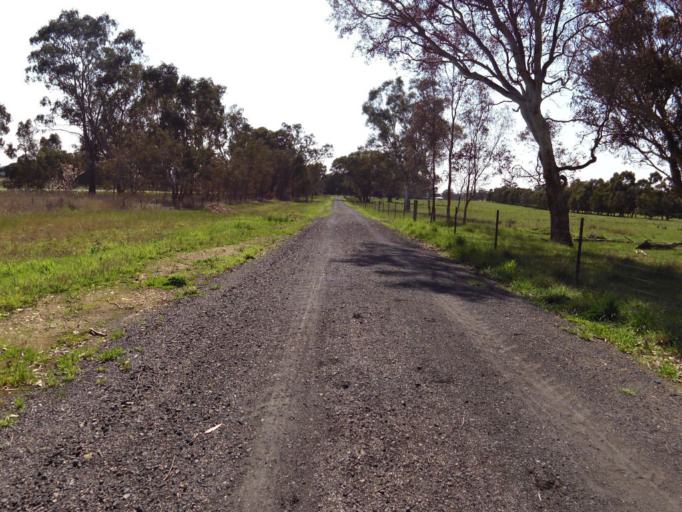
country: AU
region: Victoria
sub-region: Murrindindi
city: Alexandra
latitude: -37.1143
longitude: 145.6074
